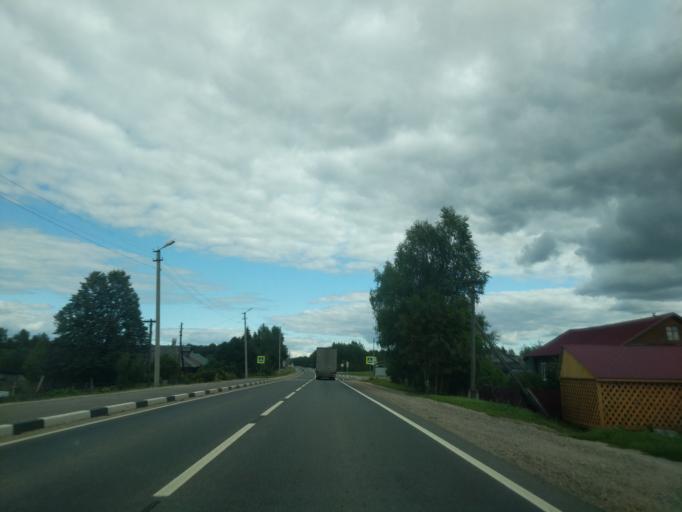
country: RU
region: Kostroma
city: Ostrovskoye
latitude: 57.8207
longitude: 42.1983
